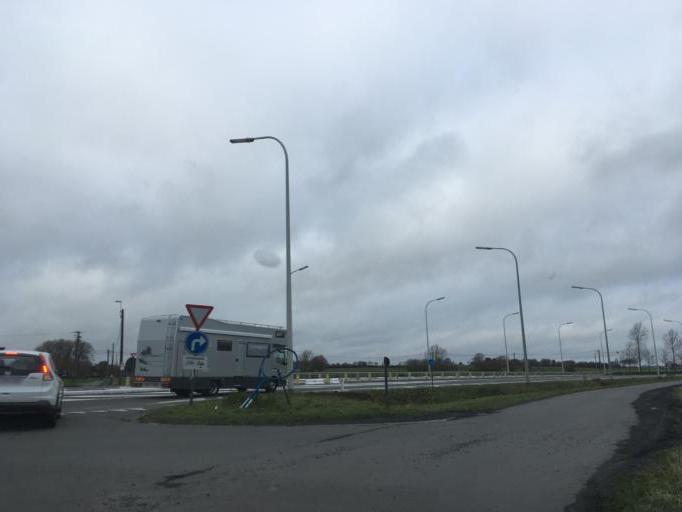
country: BE
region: Flanders
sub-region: Provincie West-Vlaanderen
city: Hooglede
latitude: 50.9734
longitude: 3.1047
